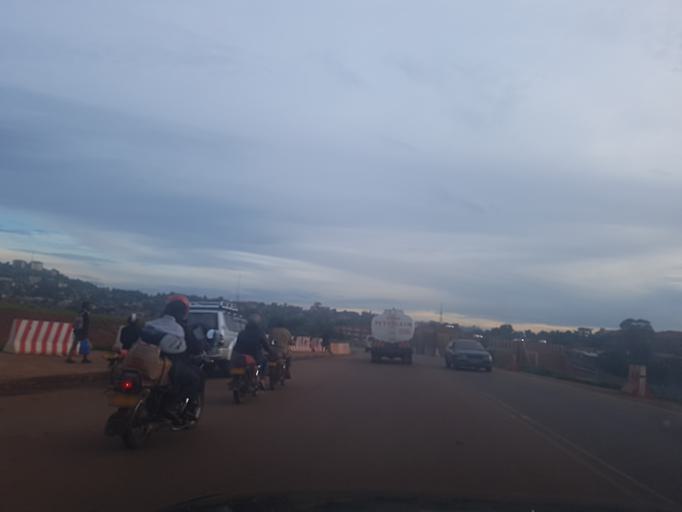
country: UG
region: Central Region
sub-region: Wakiso District
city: Kireka
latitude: 0.3645
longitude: 32.6038
